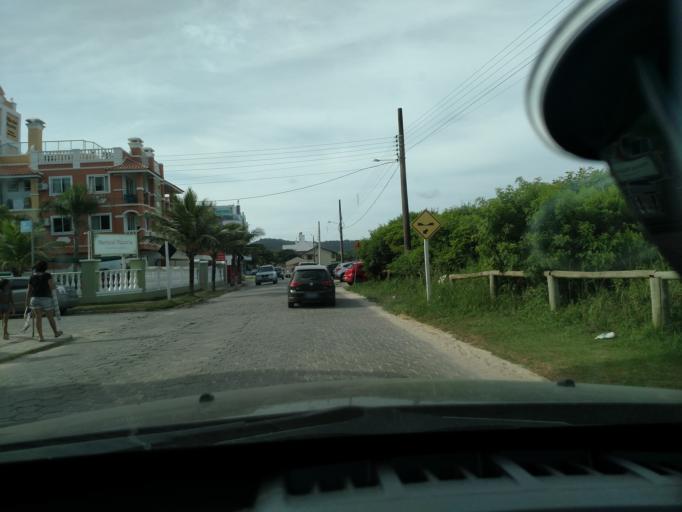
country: BR
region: Santa Catarina
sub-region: Porto Belo
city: Porto Belo
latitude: -27.1847
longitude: -48.5002
